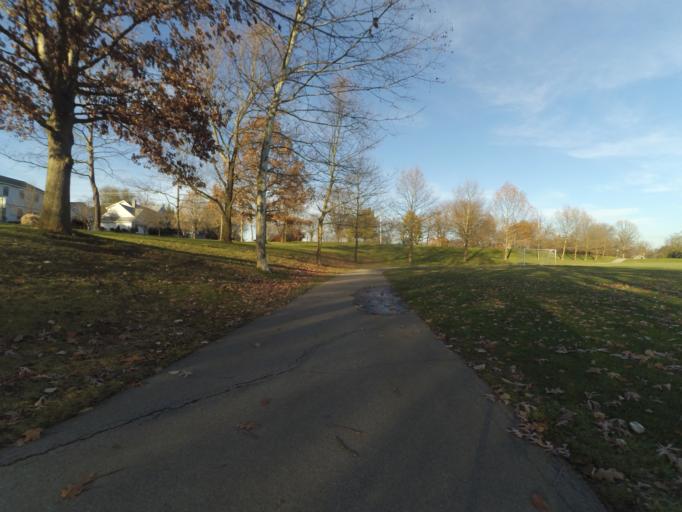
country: US
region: Pennsylvania
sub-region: Centre County
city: State College
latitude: 40.7738
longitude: -77.8652
